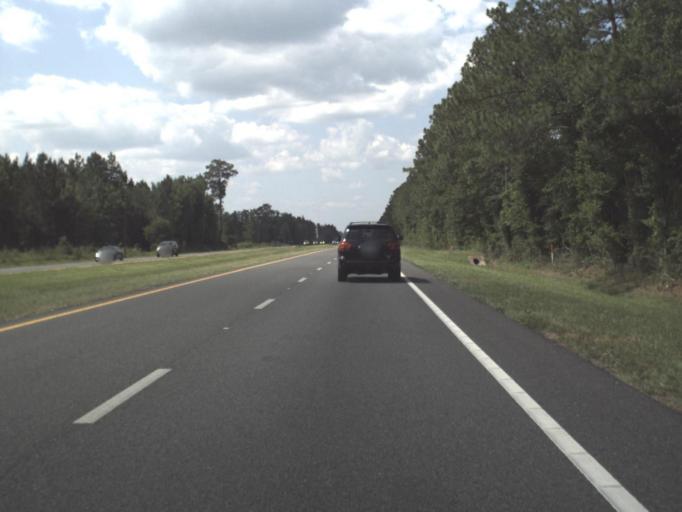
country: US
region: Florida
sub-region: Alachua County
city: Waldo
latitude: 29.7369
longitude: -82.1410
